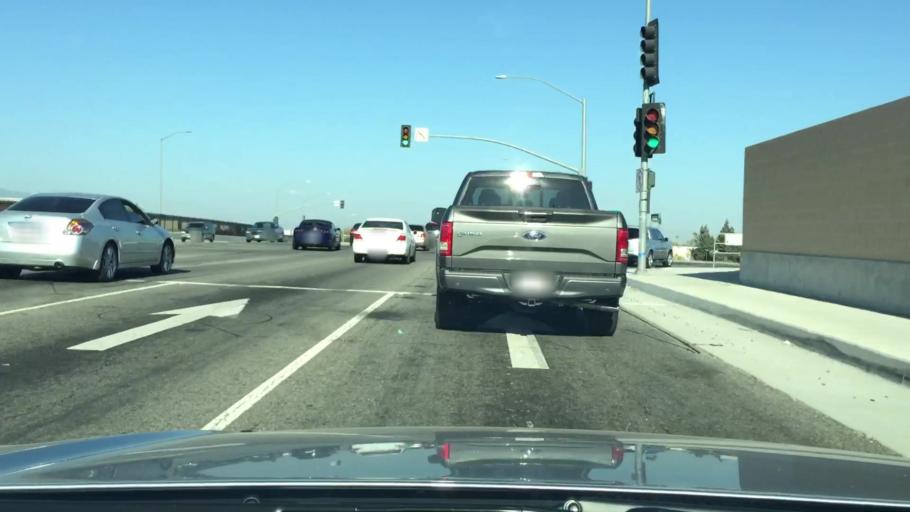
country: US
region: California
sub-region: Los Angeles County
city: Pomona
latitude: 34.0532
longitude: -117.7823
